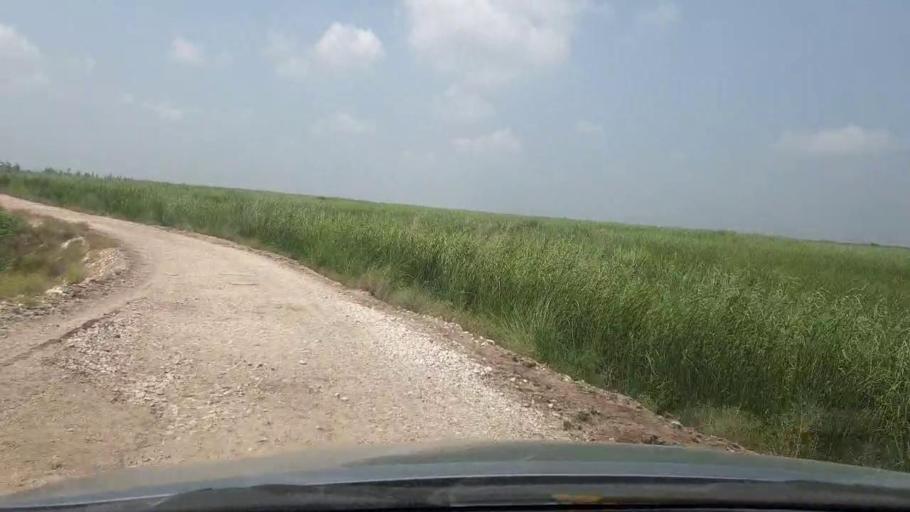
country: PK
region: Sindh
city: Khairpur
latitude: 27.4831
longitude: 68.7077
